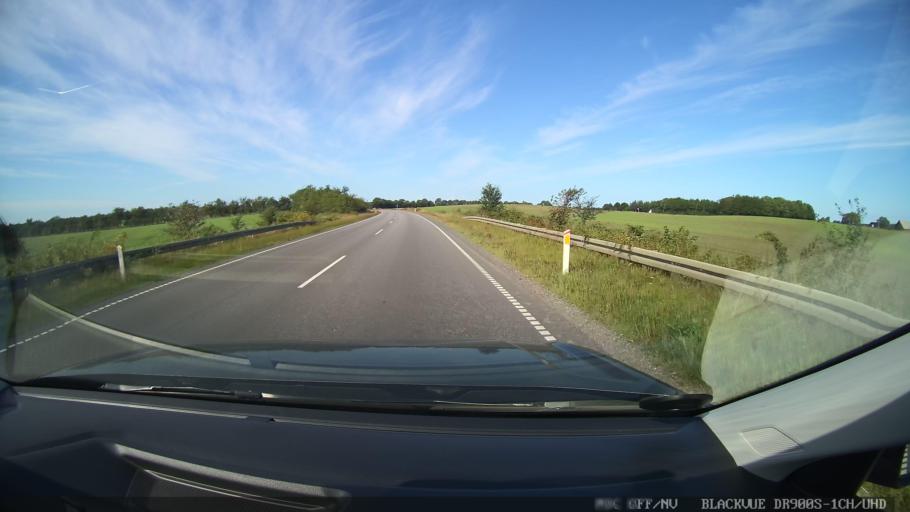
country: DK
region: North Denmark
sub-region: Mariagerfjord Kommune
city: Hobro
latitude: 56.6667
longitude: 9.7640
